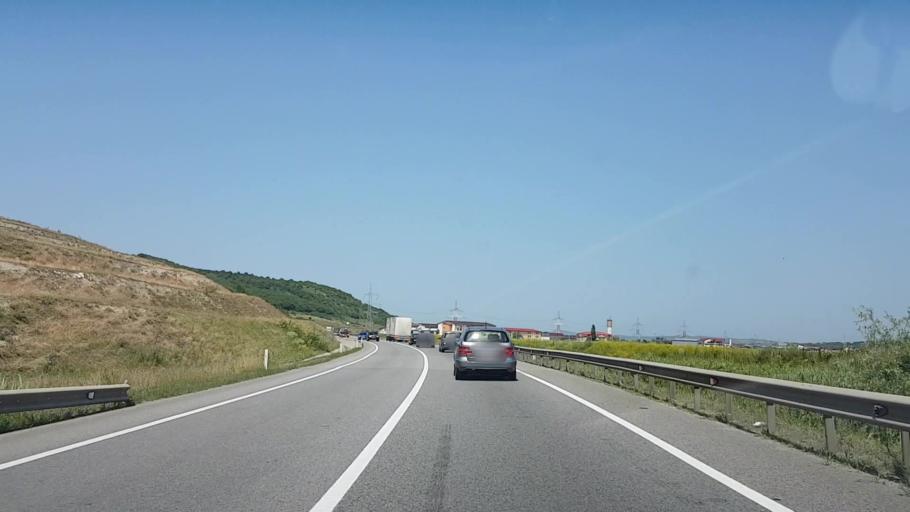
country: RO
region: Cluj
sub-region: Comuna Apahida
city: Apahida
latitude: 46.8081
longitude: 23.7346
